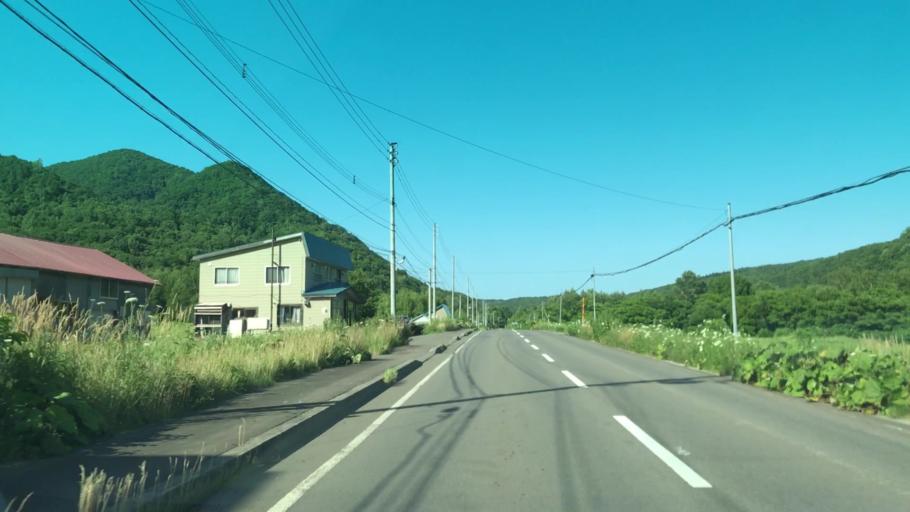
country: JP
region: Hokkaido
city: Yoichi
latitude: 43.0548
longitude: 140.8621
